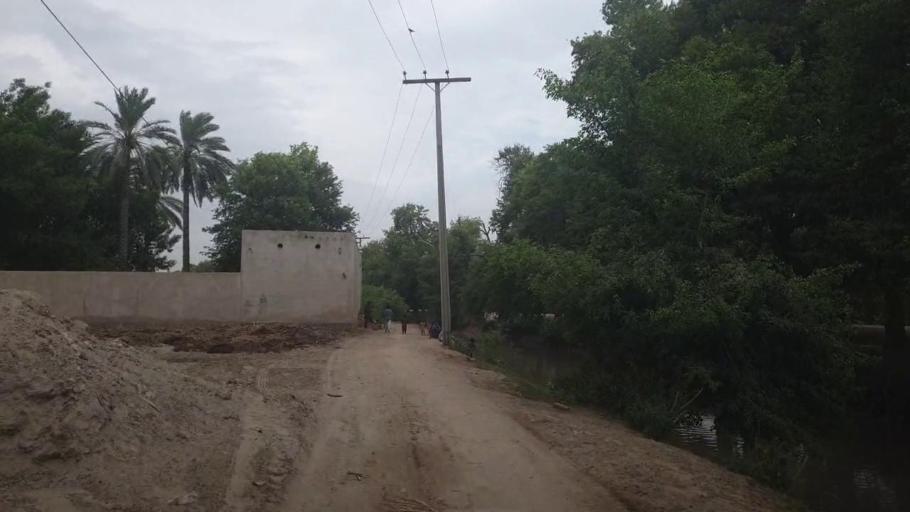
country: PK
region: Sindh
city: Khairpur
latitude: 27.6223
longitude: 68.7613
